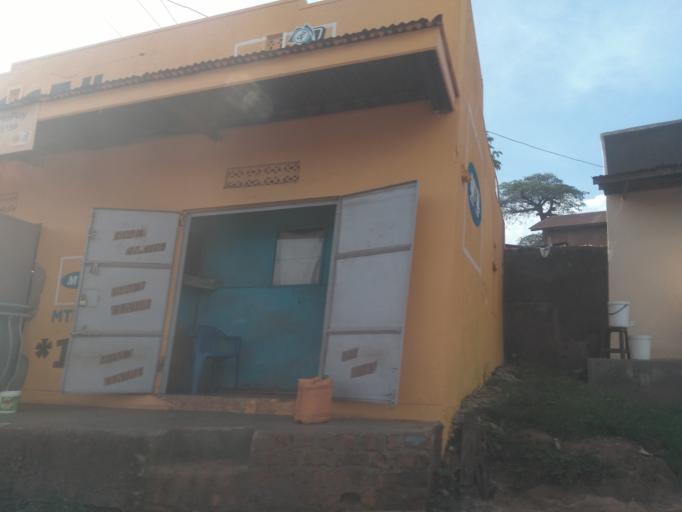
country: UG
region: Central Region
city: Kampala Central Division
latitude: 0.3547
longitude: 32.5686
